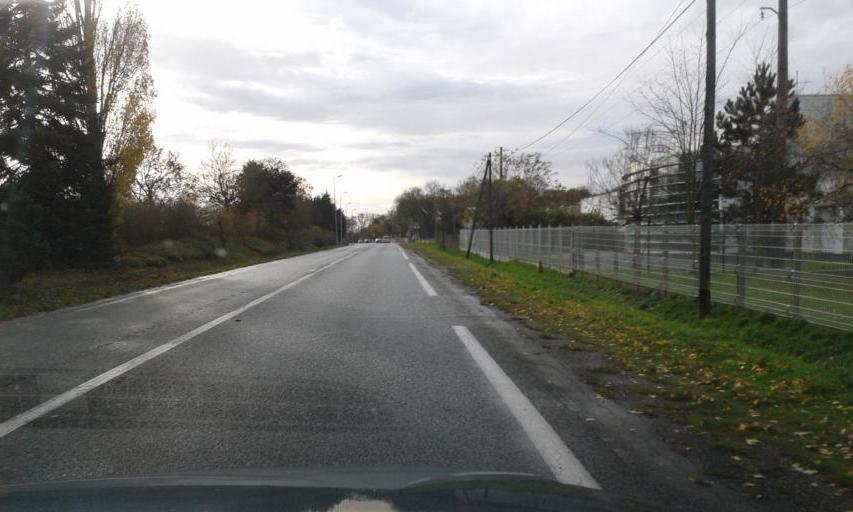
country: FR
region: Centre
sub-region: Departement du Loiret
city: Meung-sur-Loire
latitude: 47.8399
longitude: 1.7134
